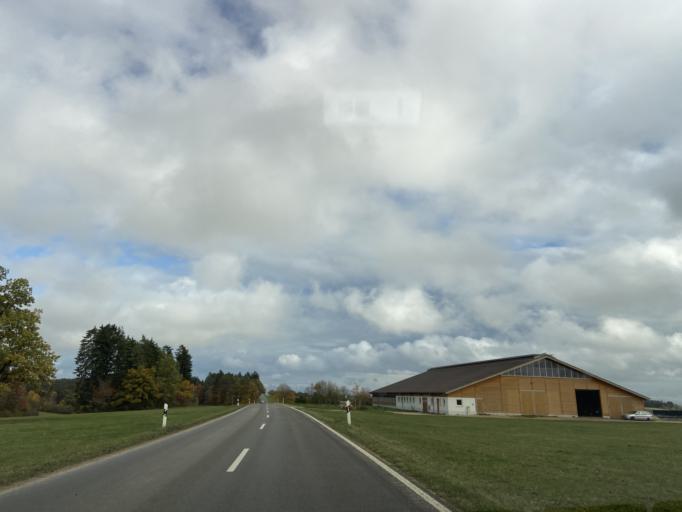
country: DE
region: Baden-Wuerttemberg
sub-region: Tuebingen Region
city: Messkirch
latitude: 48.0455
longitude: 9.1071
